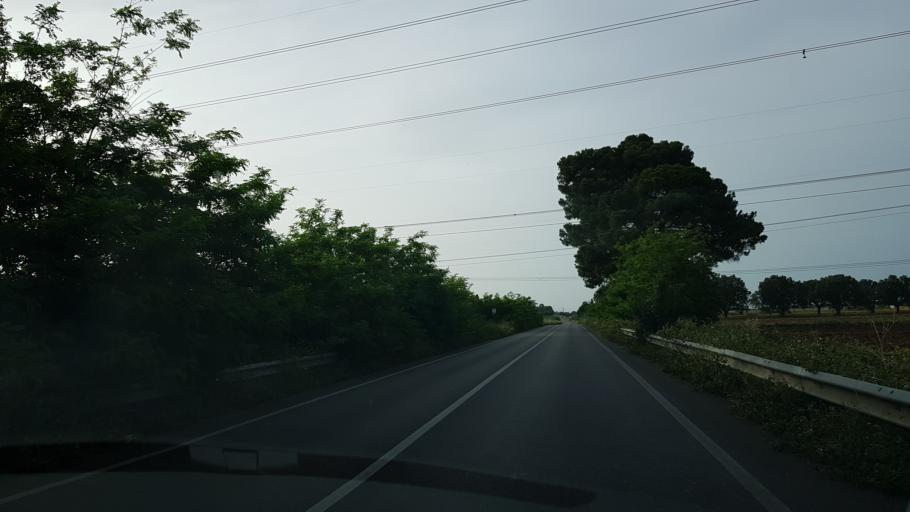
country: IT
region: Apulia
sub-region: Provincia di Brindisi
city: Tuturano
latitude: 40.5594
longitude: 17.9727
